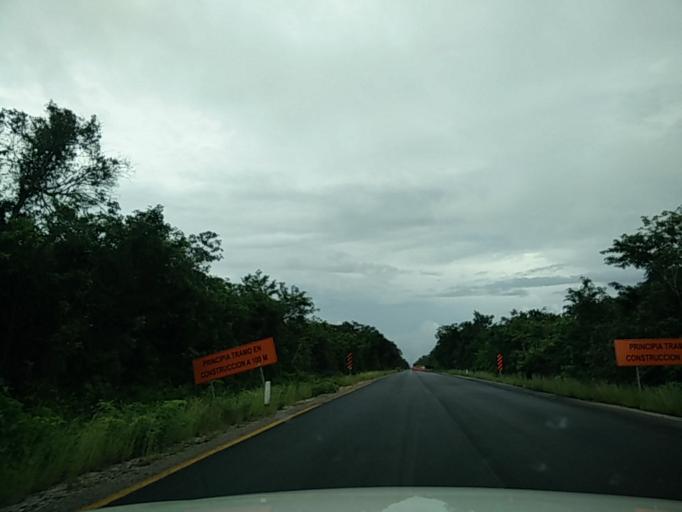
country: MX
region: Quintana Roo
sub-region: Lazaro Cardenas
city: El Tintal
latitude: 20.8969
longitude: -87.4890
